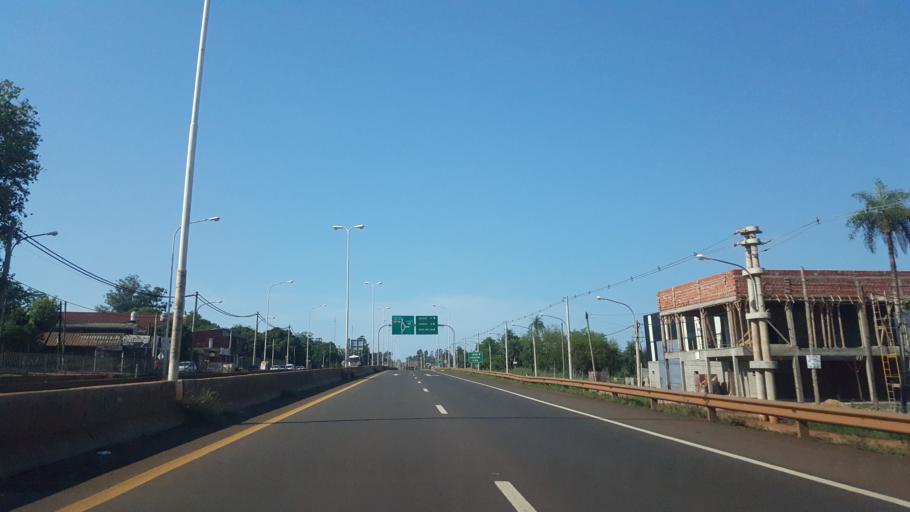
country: AR
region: Misiones
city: Garupa
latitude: -27.4576
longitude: -55.8627
